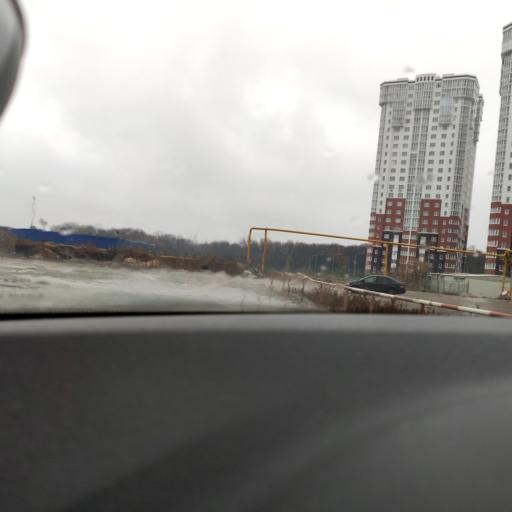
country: RU
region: Samara
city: Petra-Dubrava
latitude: 53.2766
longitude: 50.2758
